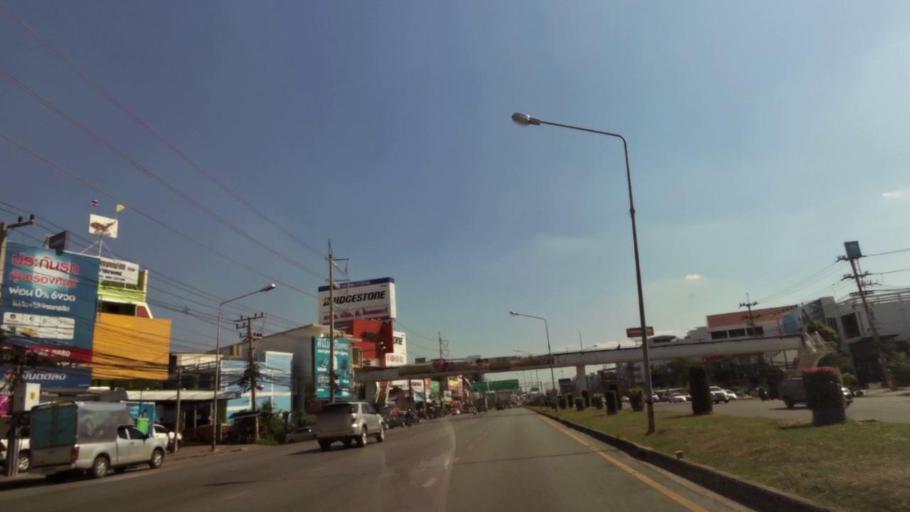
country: TH
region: Nakhon Sawan
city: Nakhon Sawan
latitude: 15.7011
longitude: 100.1175
